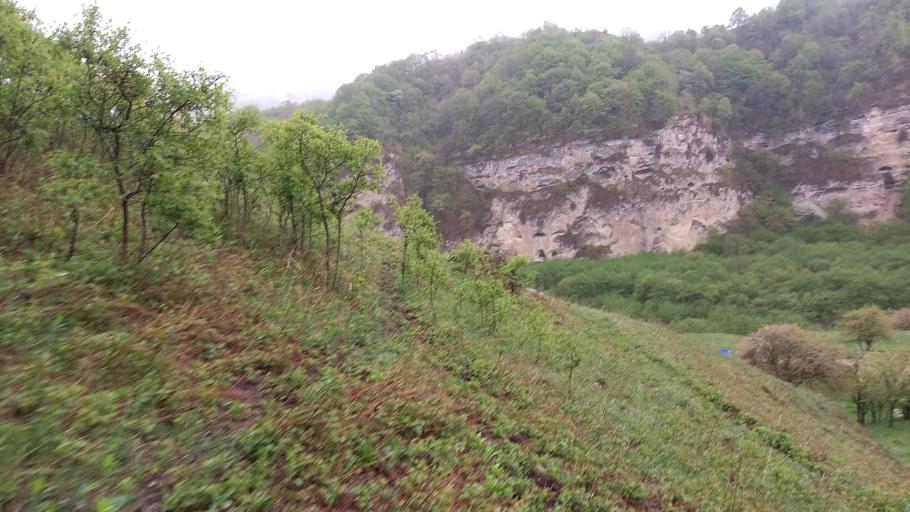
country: RU
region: Kabardino-Balkariya
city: Bylym
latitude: 43.5921
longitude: 43.0257
